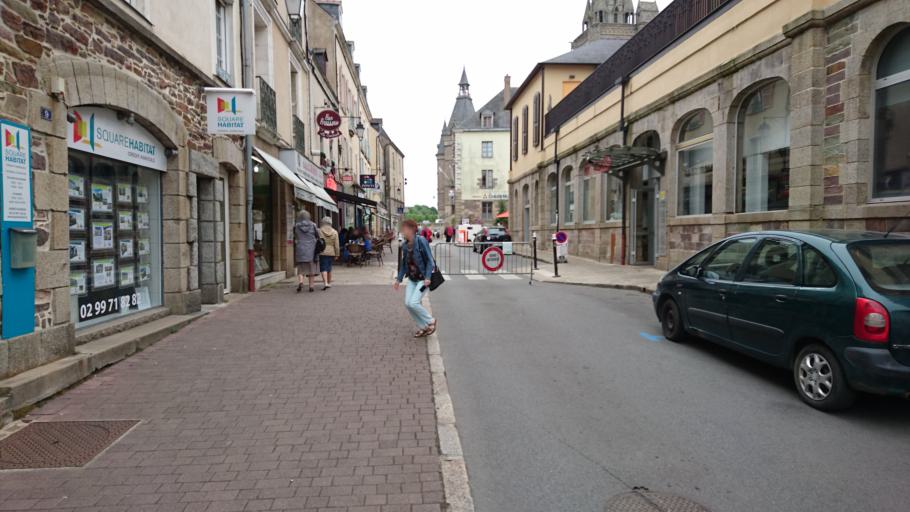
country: FR
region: Brittany
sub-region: Departement d'Ille-et-Vilaine
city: Redon
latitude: 47.6512
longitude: -2.0855
